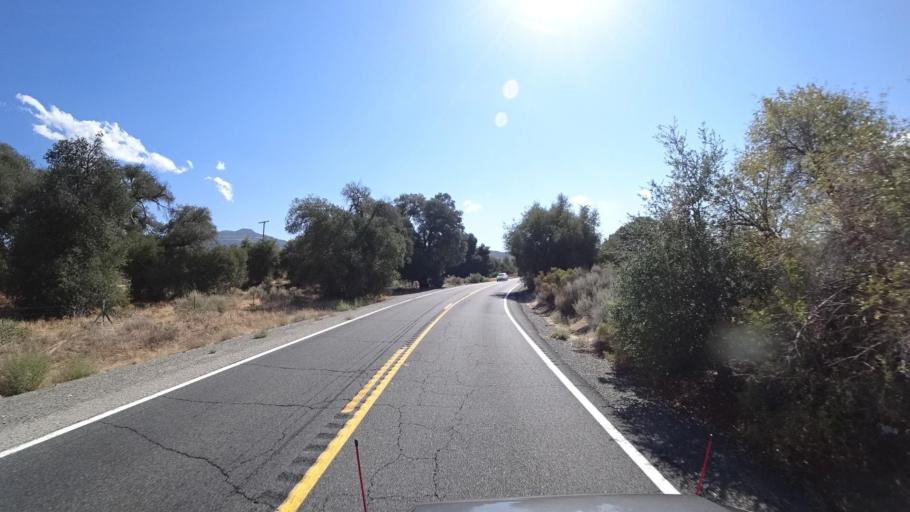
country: US
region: California
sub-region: San Diego County
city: Julian
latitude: 33.2874
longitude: -116.6462
